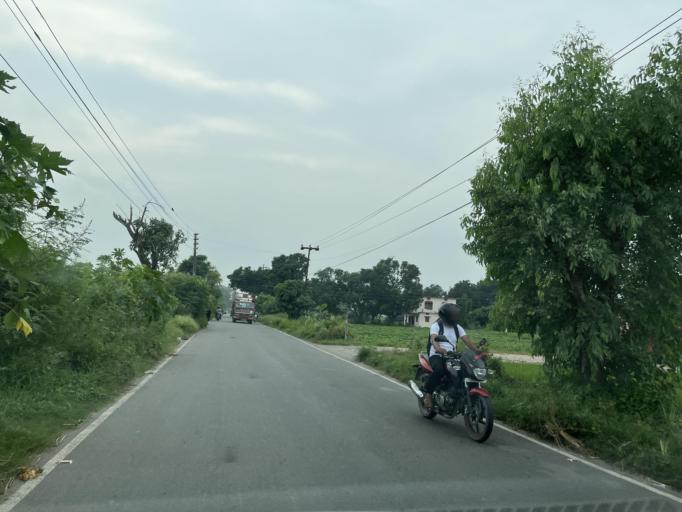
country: IN
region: Uttarakhand
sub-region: Naini Tal
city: Haldwani
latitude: 29.1729
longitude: 79.4850
